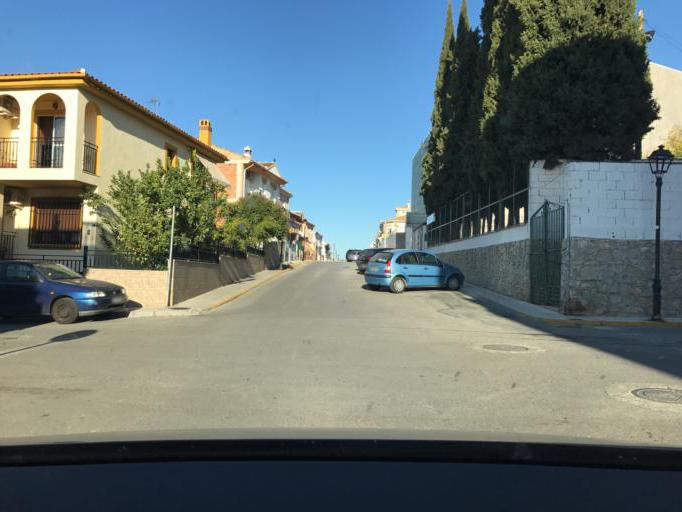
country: ES
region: Andalusia
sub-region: Provincia de Granada
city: Peligros
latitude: 37.2346
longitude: -3.6284
